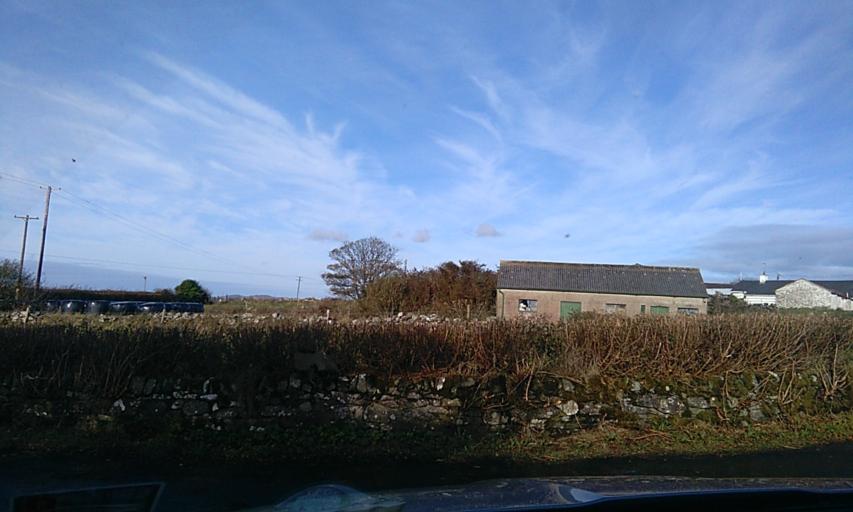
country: IE
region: Ulster
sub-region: County Donegal
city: Moville
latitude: 55.2670
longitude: -7.0542
